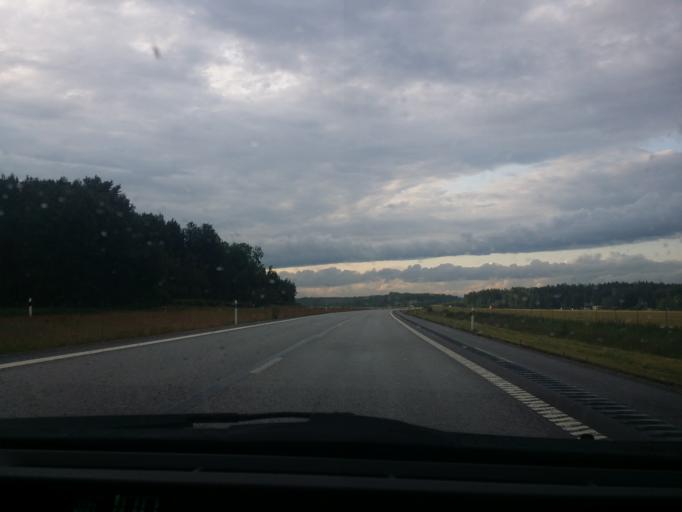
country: SE
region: Vaestmanland
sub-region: Arboga Kommun
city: Arboga
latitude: 59.4509
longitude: 15.8985
